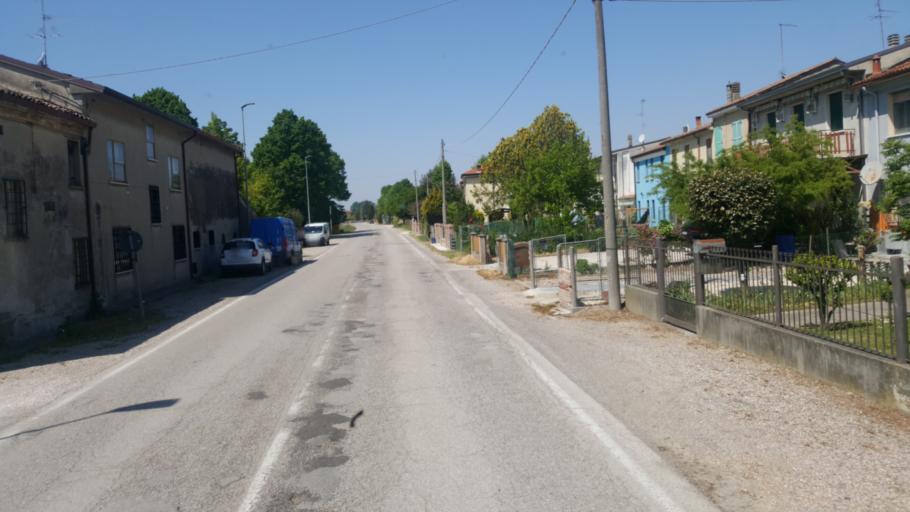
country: IT
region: Lombardy
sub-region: Provincia di Mantova
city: Sermide
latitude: 44.9921
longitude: 11.3140
